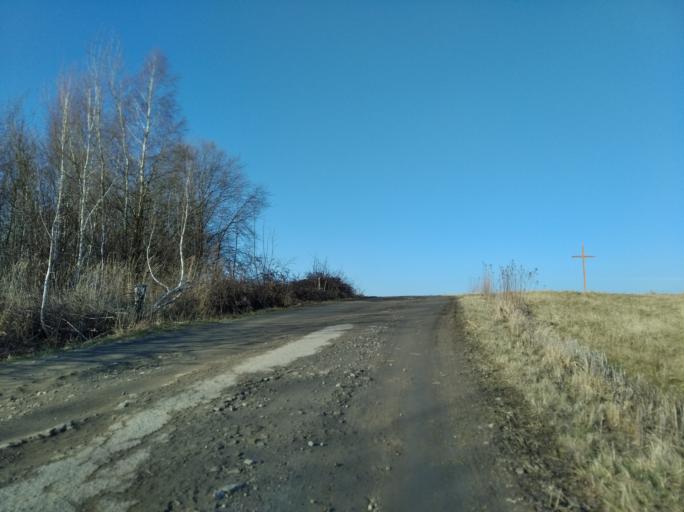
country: PL
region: Subcarpathian Voivodeship
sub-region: Powiat strzyzowski
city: Jawornik
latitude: 49.8293
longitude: 21.8703
